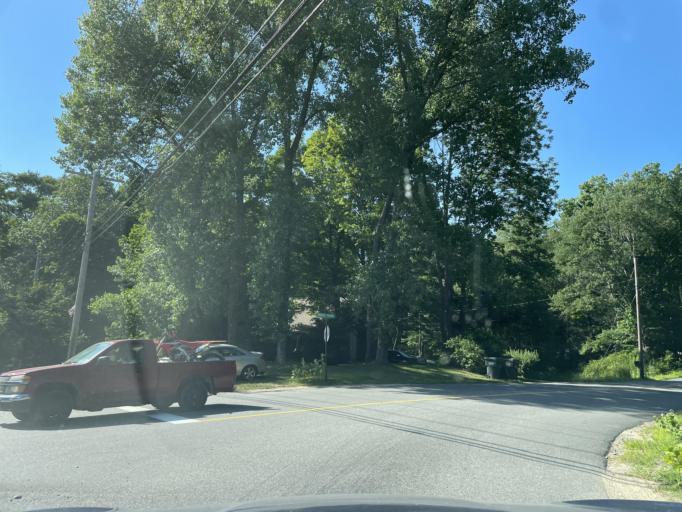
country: US
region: Massachusetts
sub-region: Worcester County
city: Charlton
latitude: 42.1345
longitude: -71.9416
